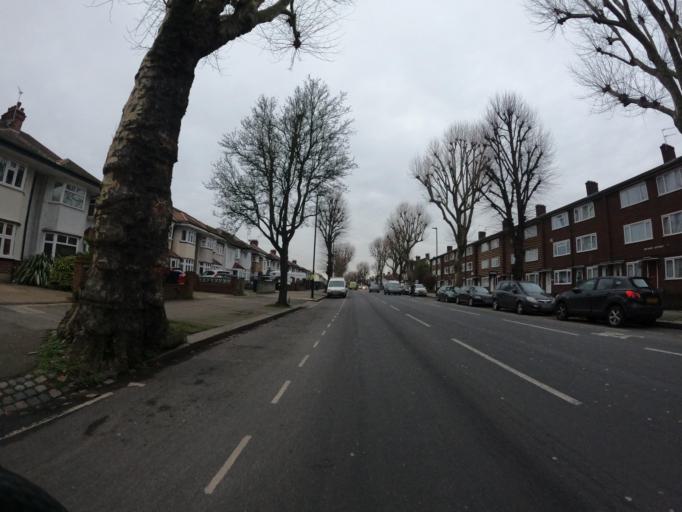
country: GB
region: England
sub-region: Greater London
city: Brentford
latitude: 51.4974
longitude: -0.3264
